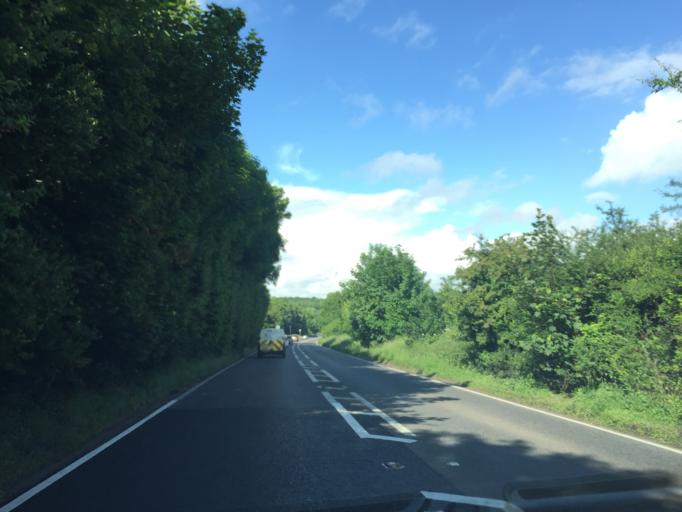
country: GB
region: England
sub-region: Dorset
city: Dorchester
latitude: 50.7308
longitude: -2.4033
